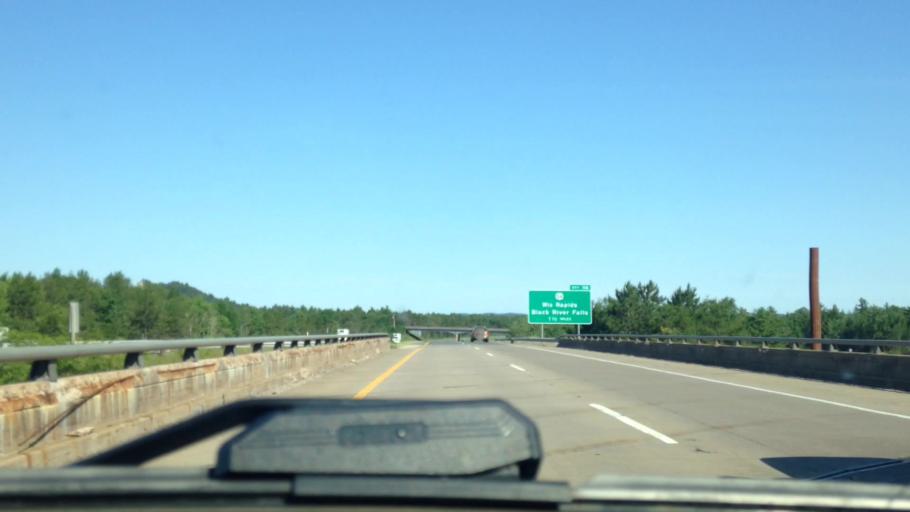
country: US
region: Wisconsin
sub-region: Jackson County
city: Black River Falls
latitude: 44.2756
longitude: -90.7983
